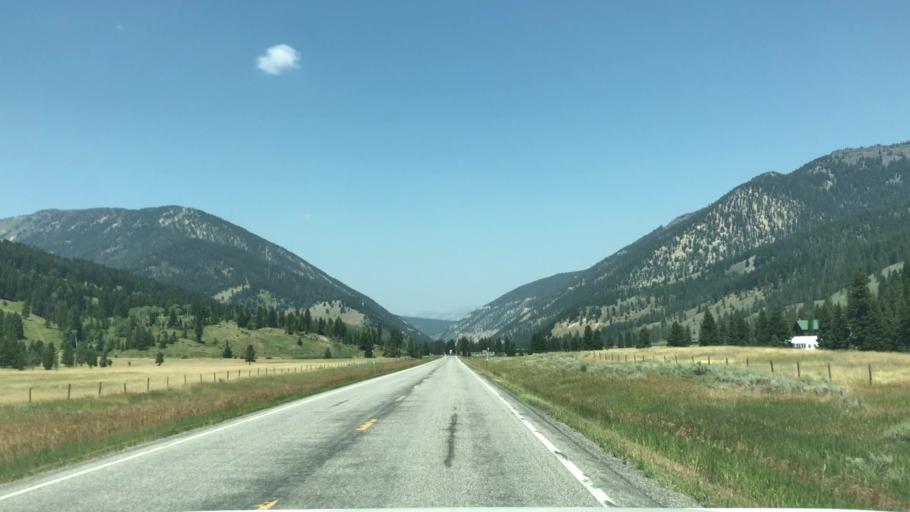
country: US
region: Montana
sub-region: Gallatin County
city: Big Sky
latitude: 45.0946
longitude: -111.2152
